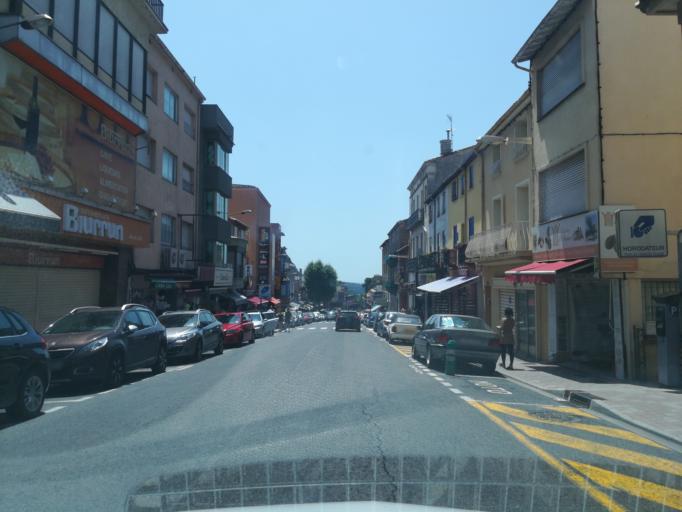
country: ES
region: Catalonia
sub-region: Provincia de Girona
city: la Jonquera
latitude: 42.4630
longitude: 2.8635
